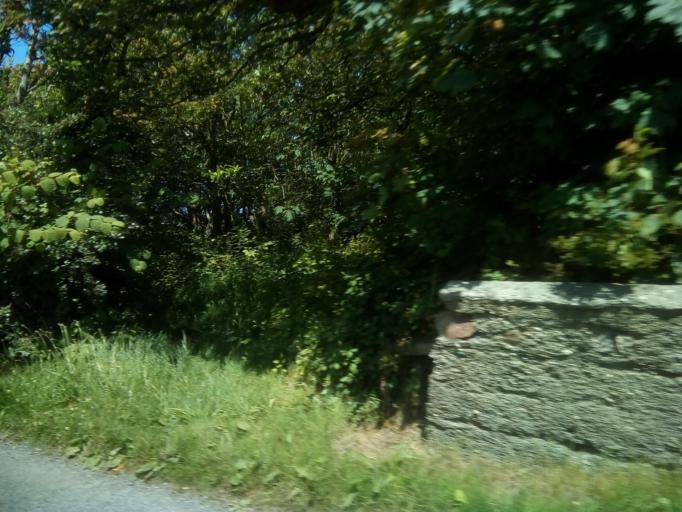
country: IE
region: Leinster
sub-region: Loch Garman
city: Loch Garman
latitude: 52.2313
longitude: -6.5551
